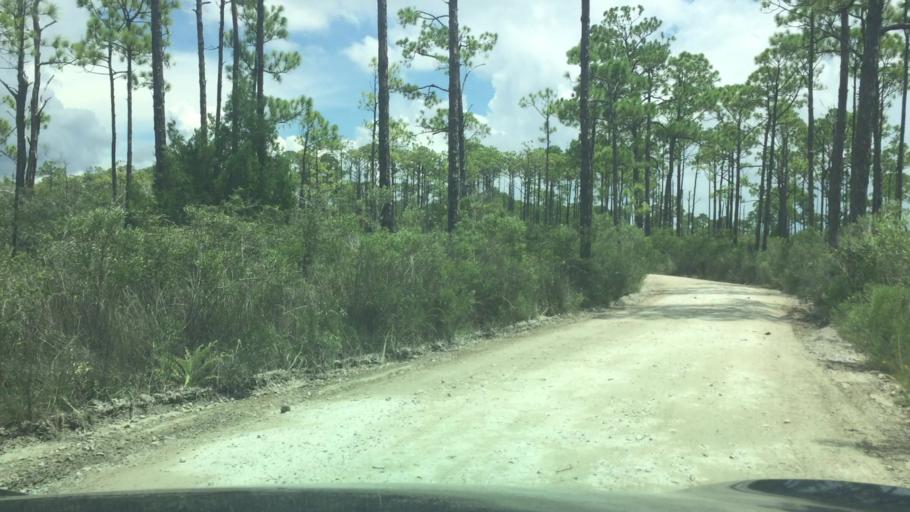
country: US
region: Florida
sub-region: Bay County
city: Mexico Beach
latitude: 29.9612
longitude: -85.4564
